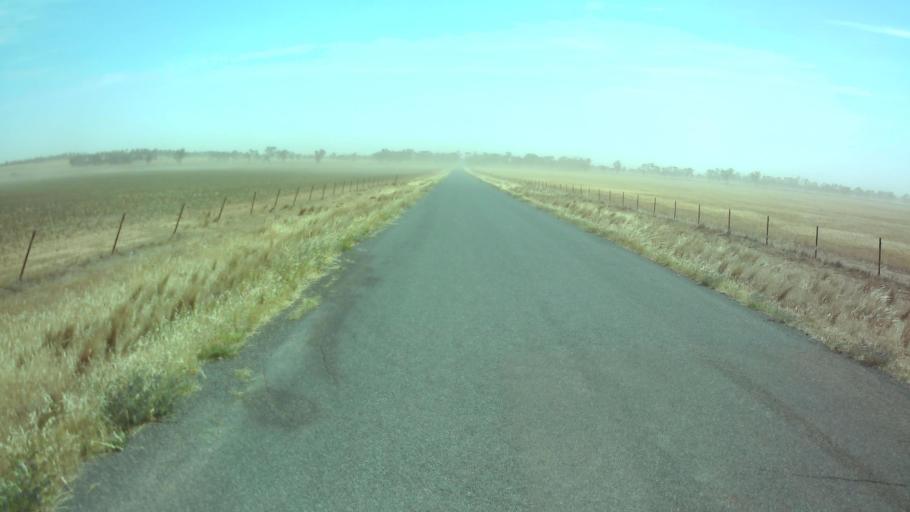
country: AU
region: New South Wales
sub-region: Weddin
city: Grenfell
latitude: -33.7270
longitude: 147.9987
